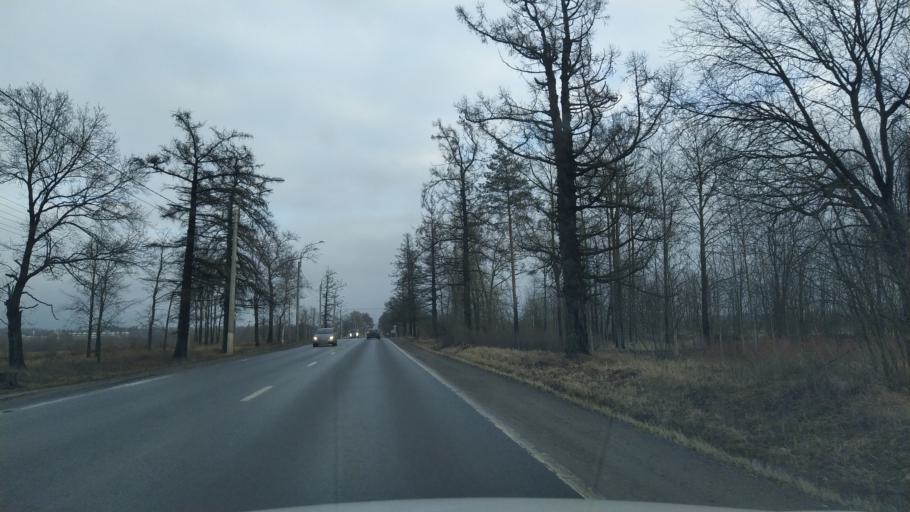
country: RU
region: St.-Petersburg
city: Aleksandrovskaya
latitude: 59.7099
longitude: 30.3209
